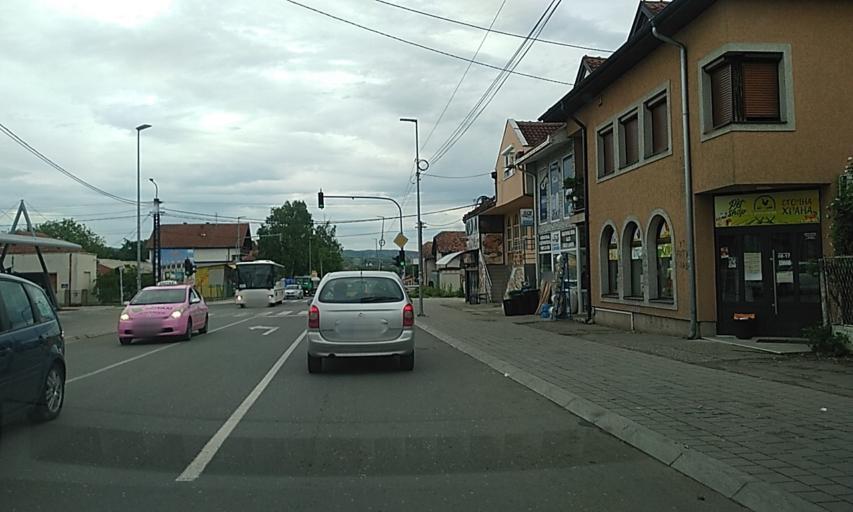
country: RS
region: Central Serbia
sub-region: Rasinski Okrug
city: Krusevac
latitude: 43.5863
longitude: 21.3395
